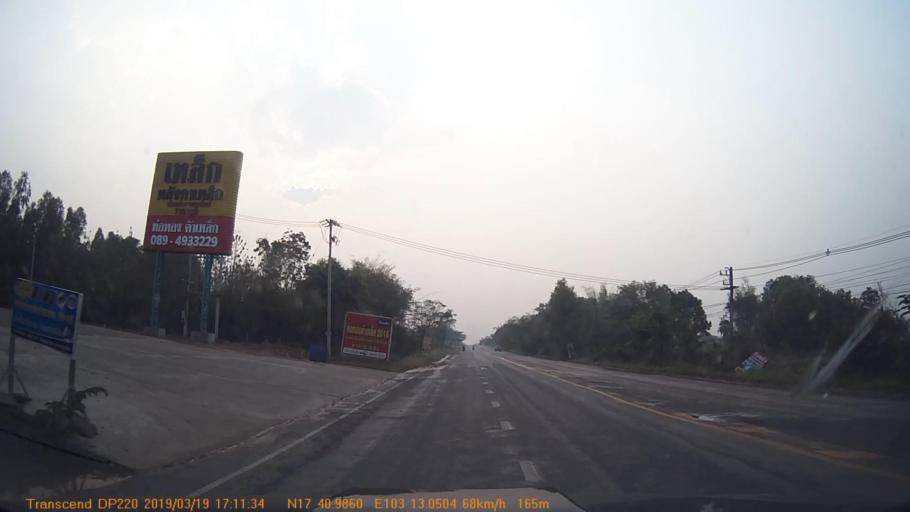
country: TH
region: Changwat Udon Thani
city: Ban Dung
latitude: 17.6832
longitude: 103.2170
